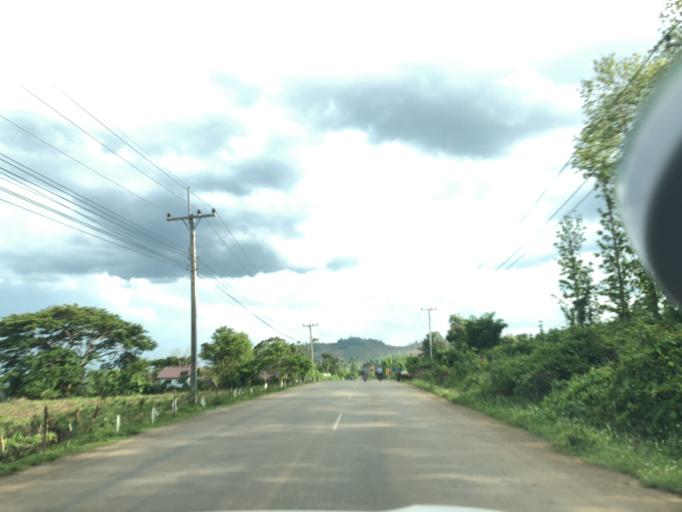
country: TH
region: Uttaradit
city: Ban Khok
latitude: 18.1435
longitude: 101.3819
